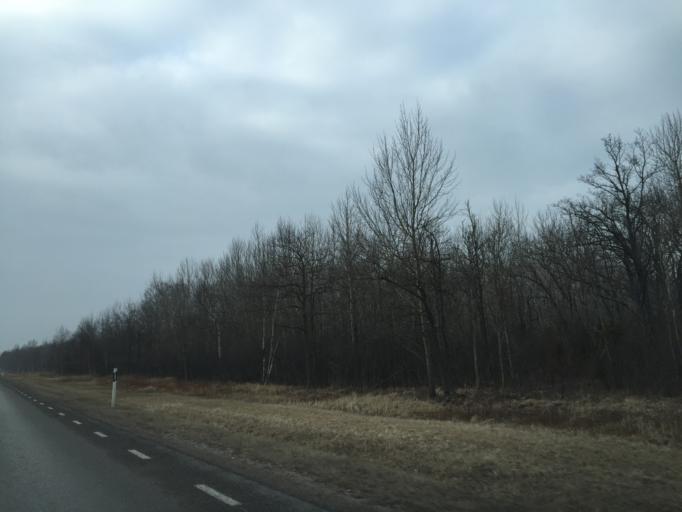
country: EE
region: Saare
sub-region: Orissaare vald
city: Orissaare
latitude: 58.5798
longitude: 23.3608
